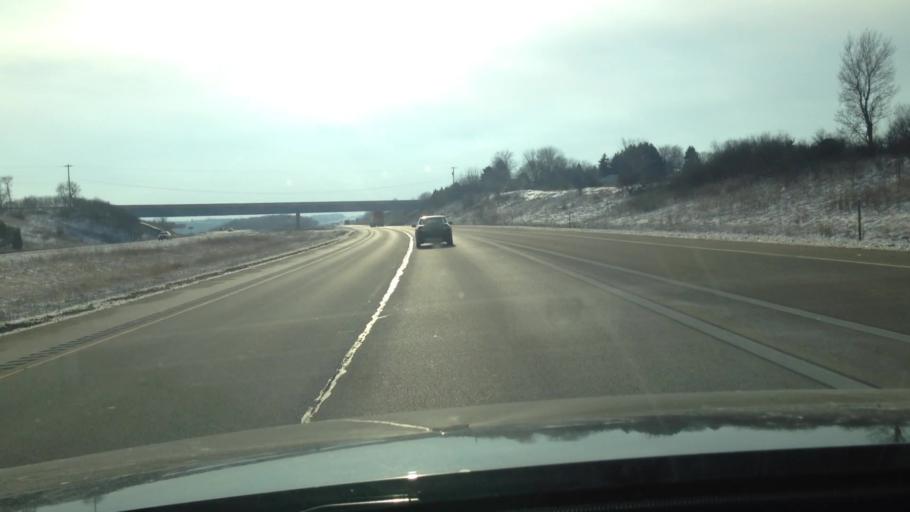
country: US
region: Wisconsin
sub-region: Walworth County
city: East Troy
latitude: 42.7447
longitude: -88.4502
